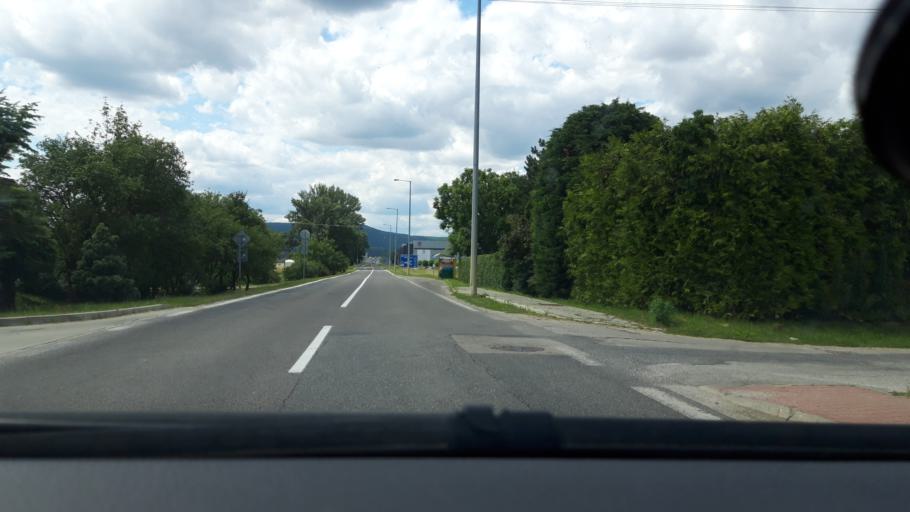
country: SK
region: Trenciansky
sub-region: Okres Nove Mesto nad Vahom
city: Nove Mesto nad Vahom
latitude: 48.7607
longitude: 17.8826
